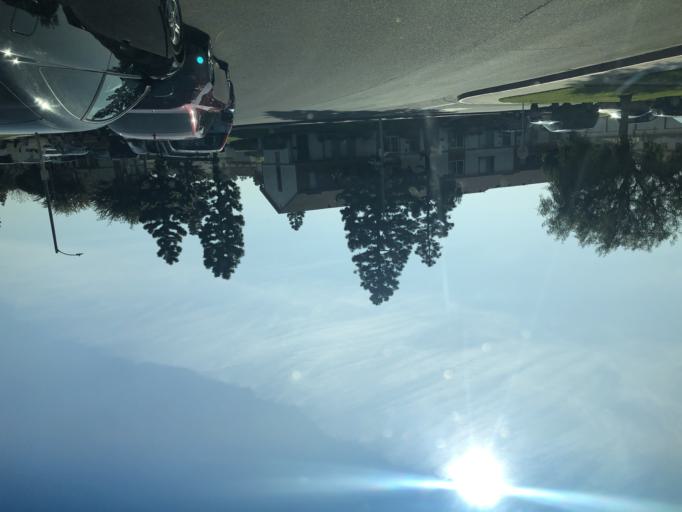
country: US
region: California
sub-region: Orange County
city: Santa Ana
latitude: 33.7080
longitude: -117.8729
